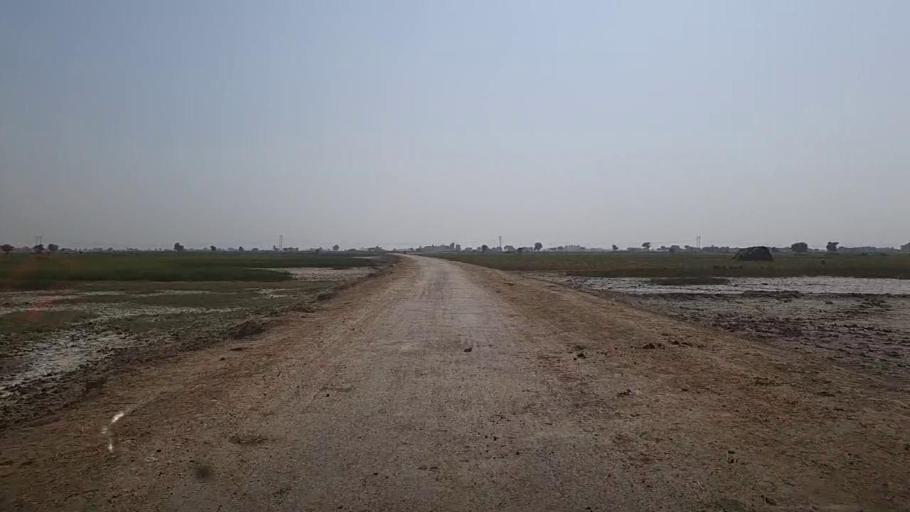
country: PK
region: Sindh
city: Kandhkot
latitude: 28.3936
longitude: 69.2933
